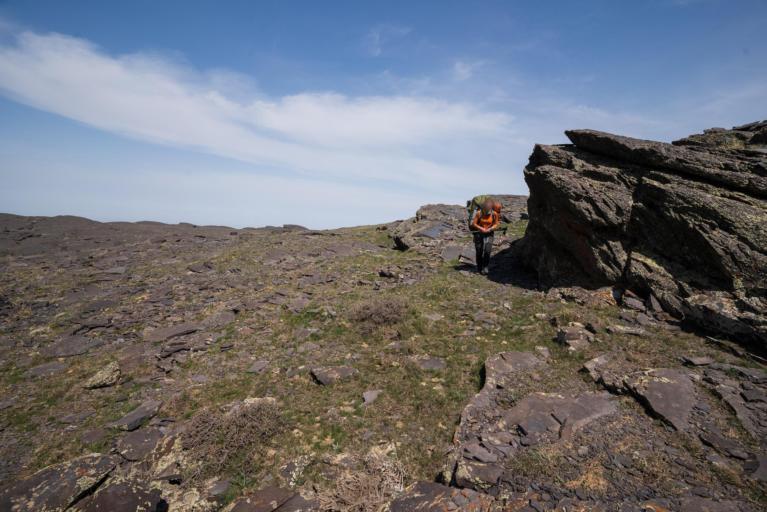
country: KZ
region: Ongtustik Qazaqstan
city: Kentau
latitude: 43.8402
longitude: 68.4857
